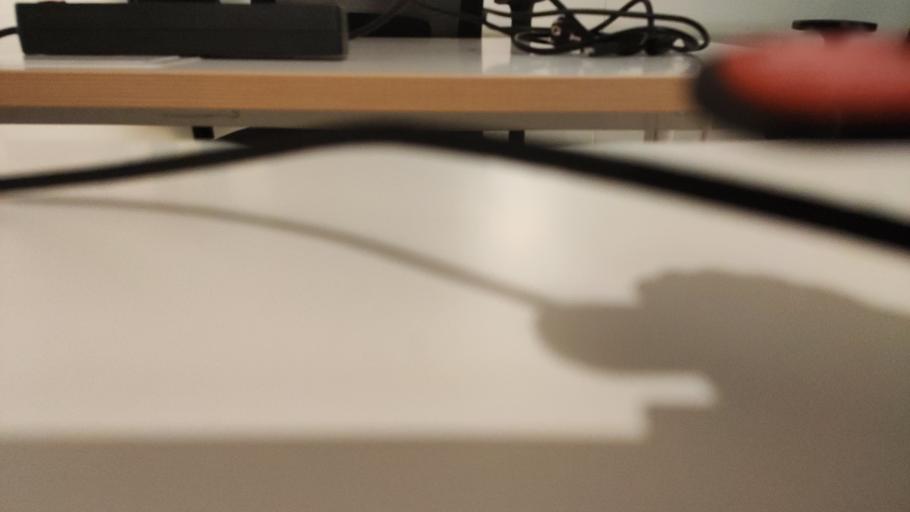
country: RU
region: Moskovskaya
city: Obolensk
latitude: 55.0021
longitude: 37.2232
